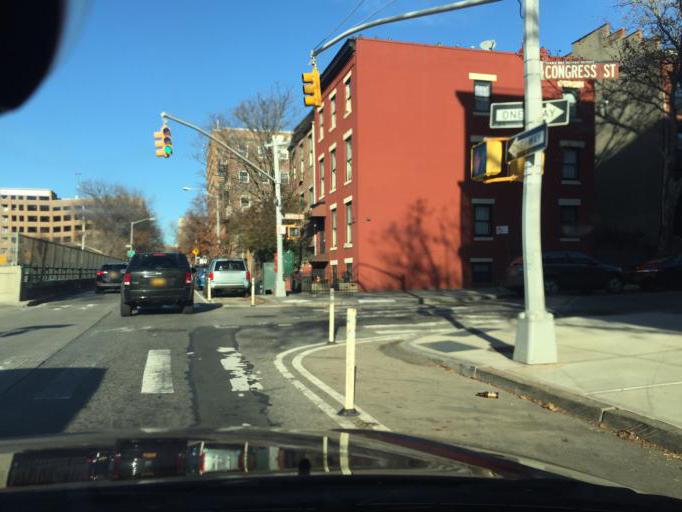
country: US
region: New York
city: New York City
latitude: 40.6890
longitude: -73.9988
